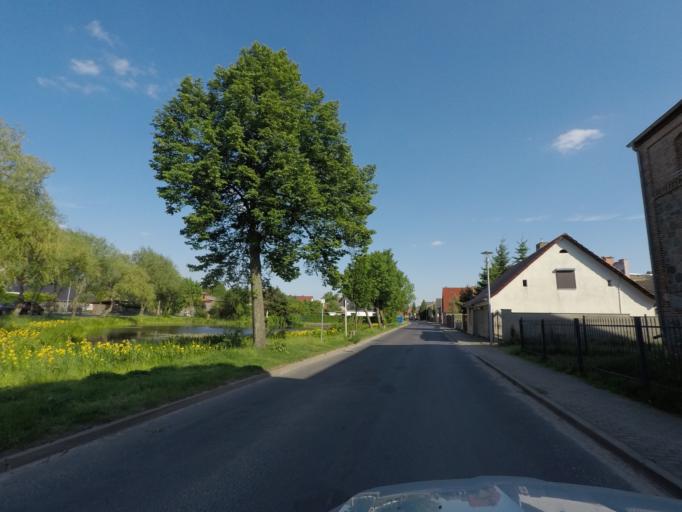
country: DE
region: Brandenburg
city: Werftpfuhl
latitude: 52.7389
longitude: 13.8350
